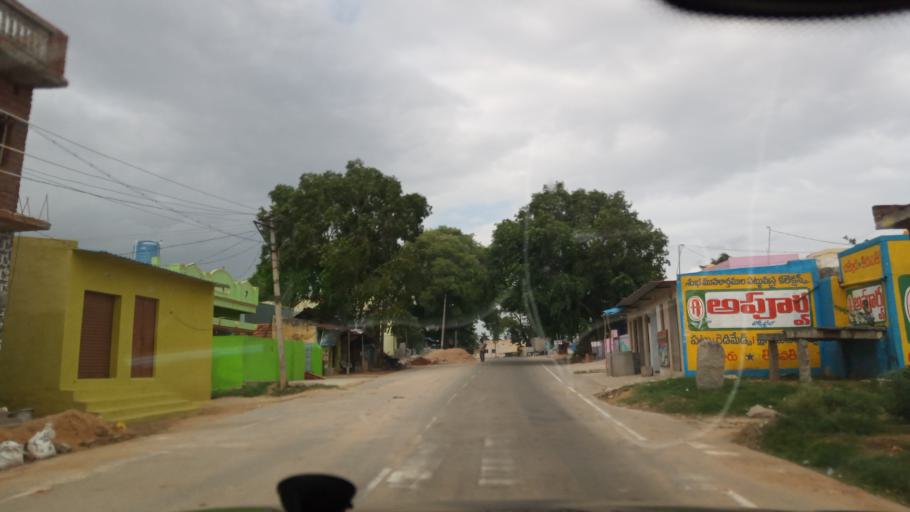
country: IN
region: Andhra Pradesh
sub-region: Chittoor
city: Palmaner
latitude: 13.1852
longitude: 78.8366
